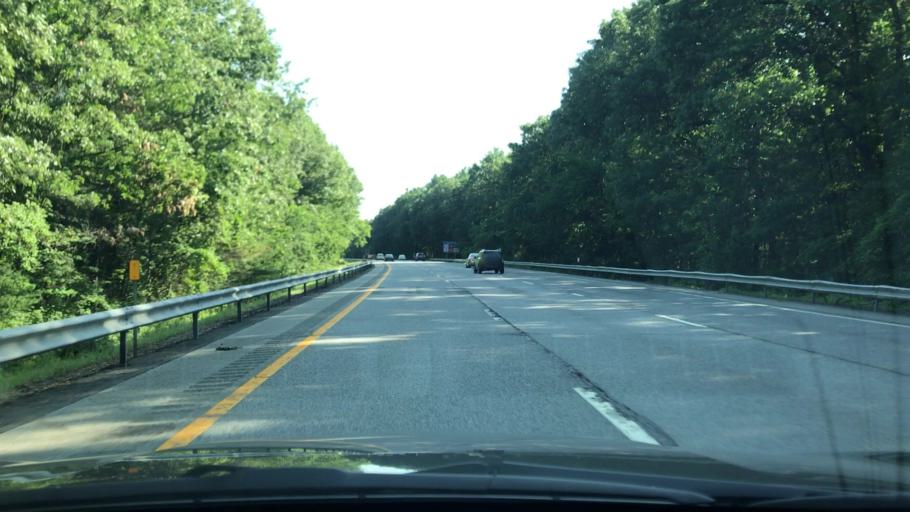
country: US
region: New York
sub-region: Saratoga County
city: Saratoga Springs
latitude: 43.1071
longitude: -73.7523
